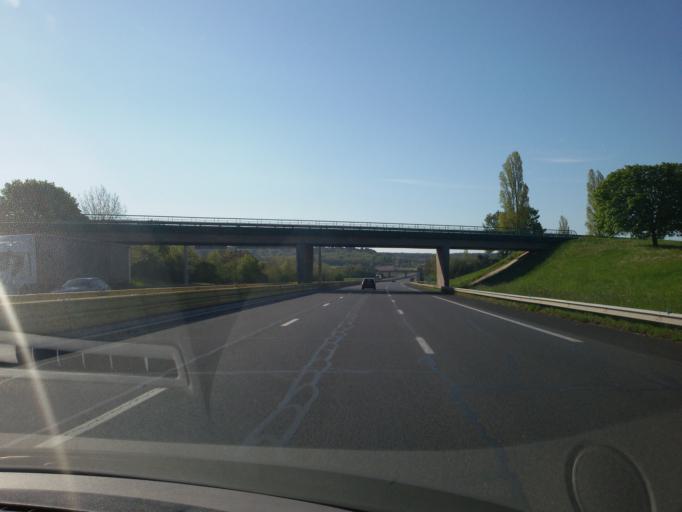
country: FR
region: Ile-de-France
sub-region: Departement de Seine-et-Marne
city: Nemours
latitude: 48.2736
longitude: 2.7124
